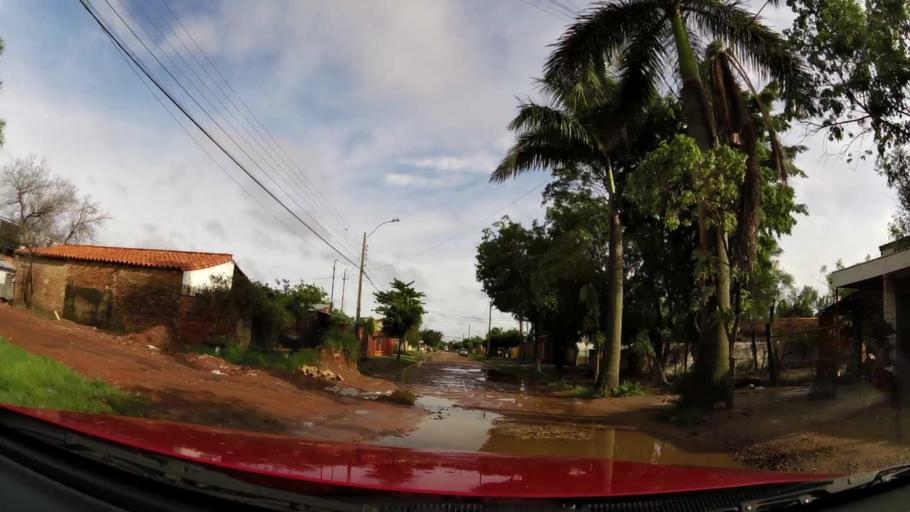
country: PY
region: Central
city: Limpio
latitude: -25.1851
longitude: -57.4881
